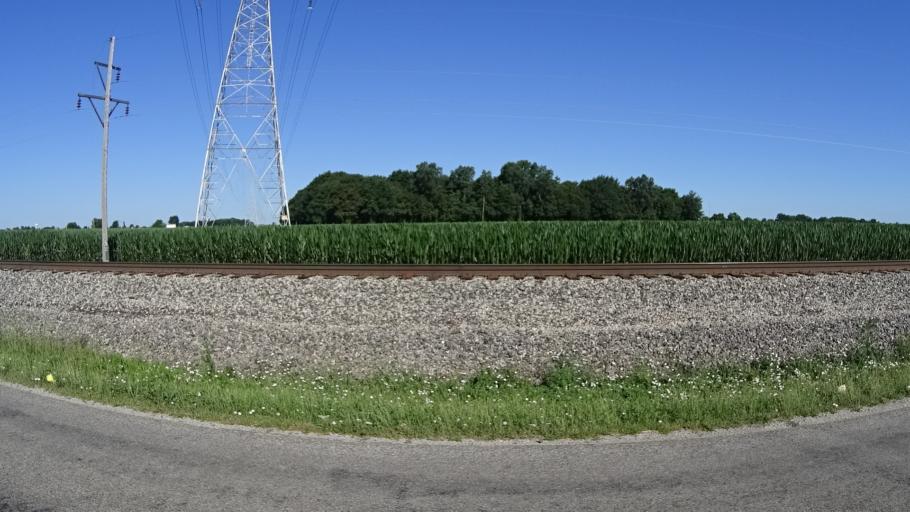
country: US
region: Ohio
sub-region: Erie County
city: Sandusky
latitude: 41.3855
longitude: -82.7596
